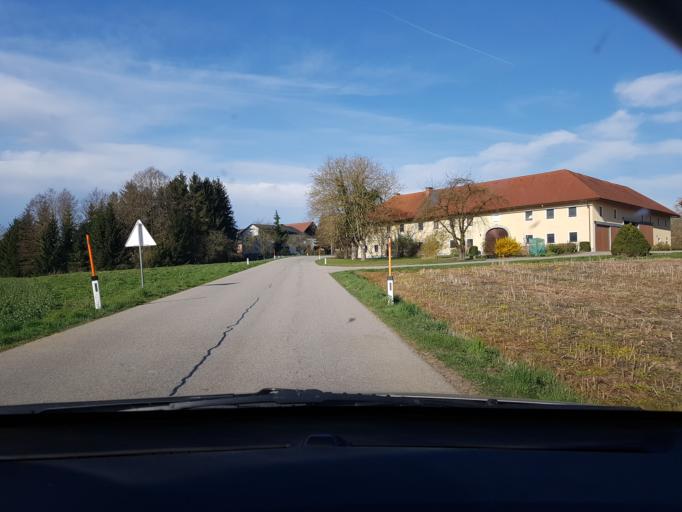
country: AT
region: Upper Austria
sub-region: Politischer Bezirk Linz-Land
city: Sankt Florian
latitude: 48.1609
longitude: 14.4011
